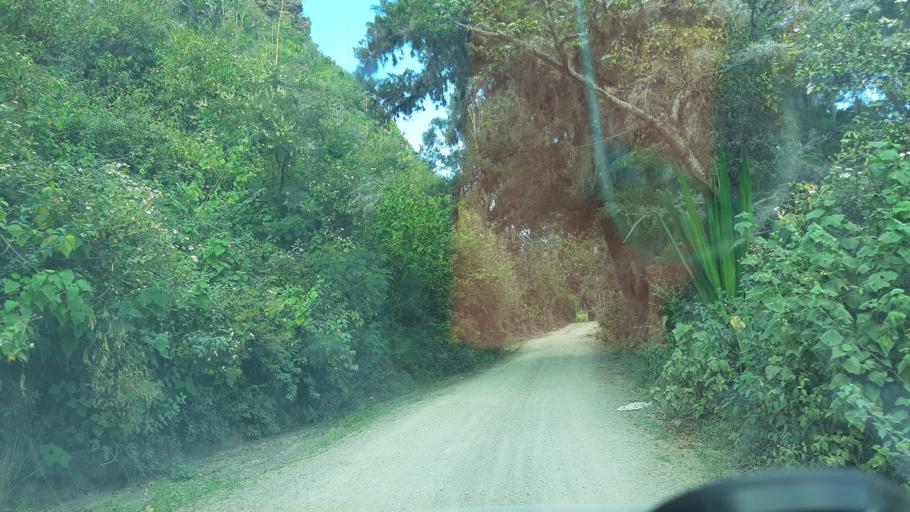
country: CO
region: Boyaca
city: Villa de Leiva
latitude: 5.6800
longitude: -73.5669
